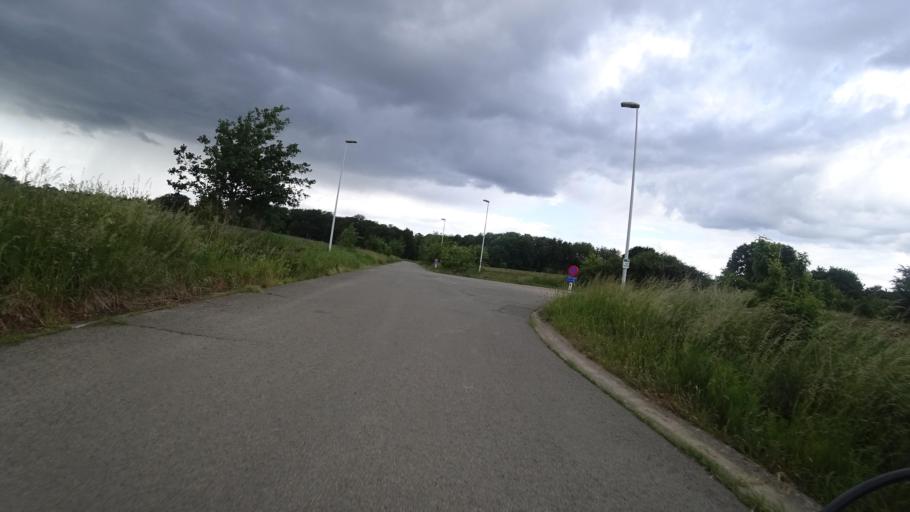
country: BE
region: Wallonia
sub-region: Province du Brabant Wallon
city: Louvain-la-Neuve
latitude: 50.6771
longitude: 4.6151
